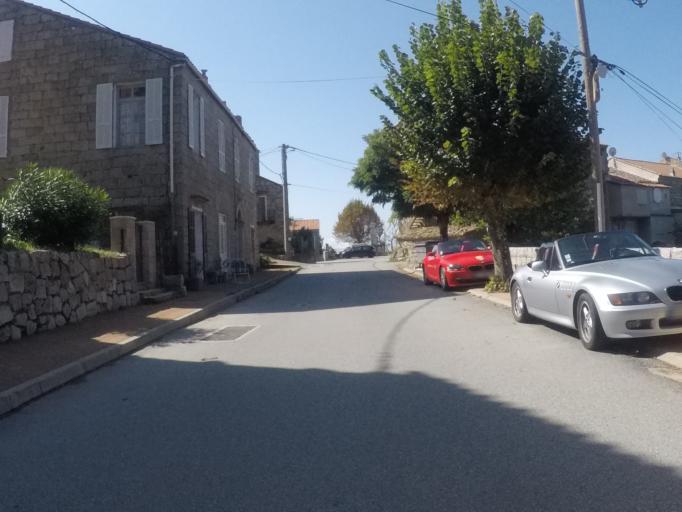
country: FR
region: Corsica
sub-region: Departement de la Corse-du-Sud
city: Zonza
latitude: 41.7697
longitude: 9.0801
